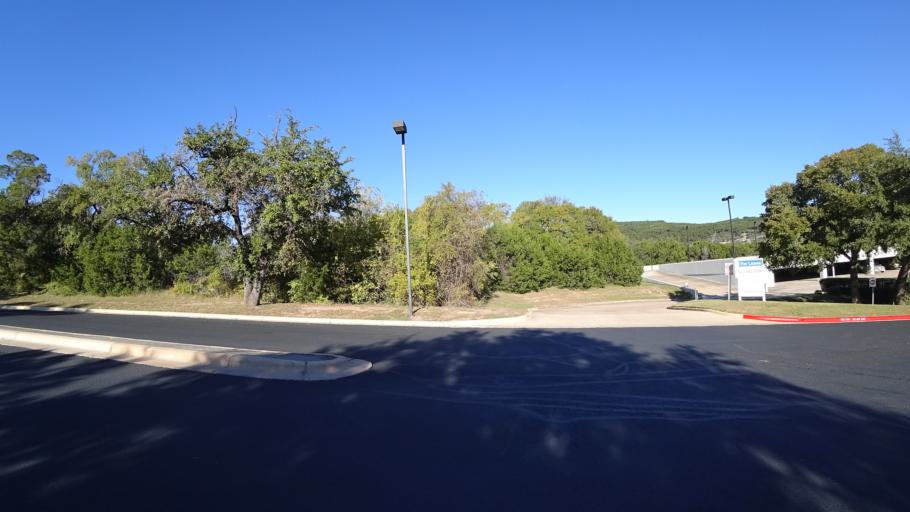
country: US
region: Texas
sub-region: Travis County
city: West Lake Hills
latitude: 30.3482
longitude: -97.8016
